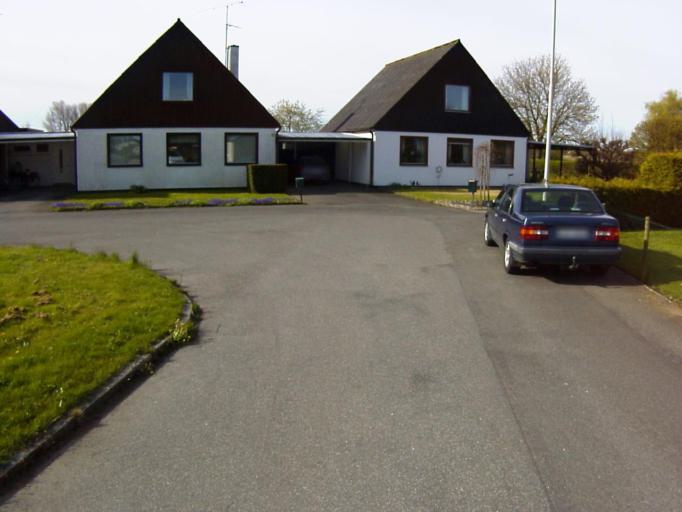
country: SE
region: Skane
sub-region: Kristianstads Kommun
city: Kristianstad
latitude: 56.0089
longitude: 14.1511
